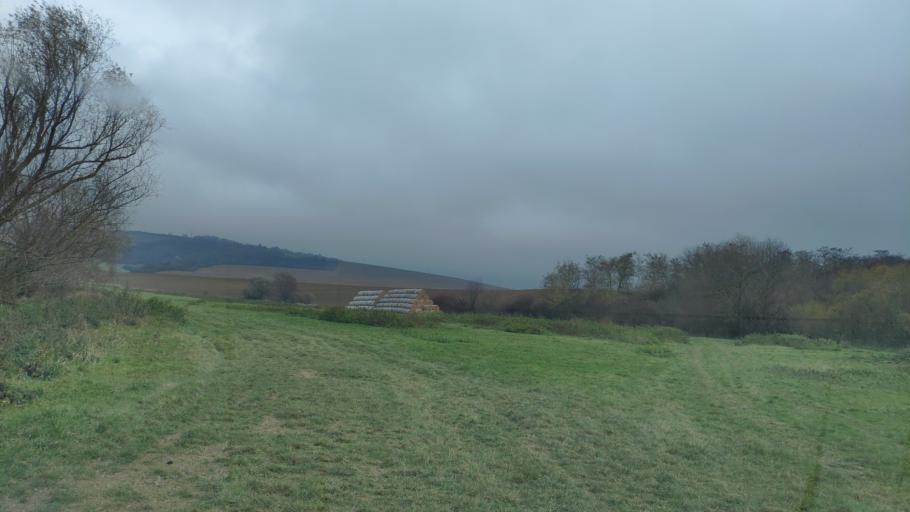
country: SK
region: Presovsky
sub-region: Okres Presov
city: Presov
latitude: 49.0125
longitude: 21.1986
